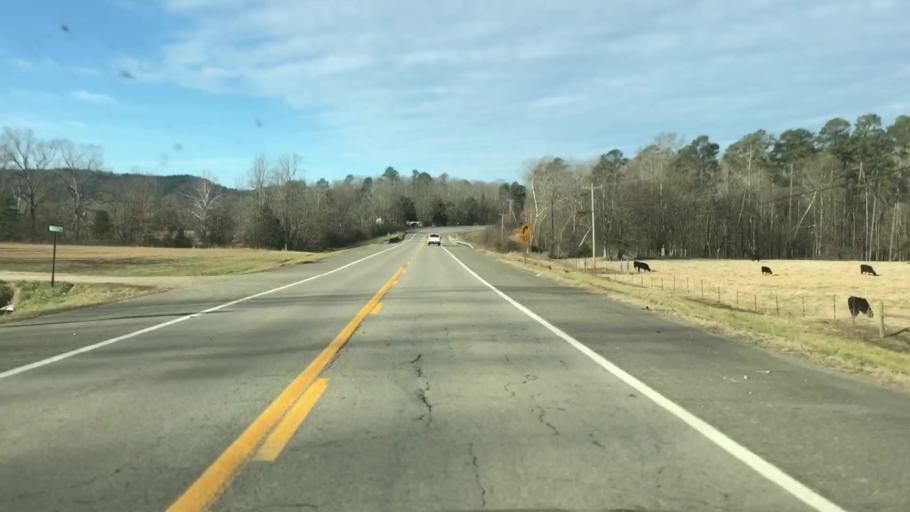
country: US
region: Arkansas
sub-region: Montgomery County
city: Mount Ida
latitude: 34.5397
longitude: -93.5989
